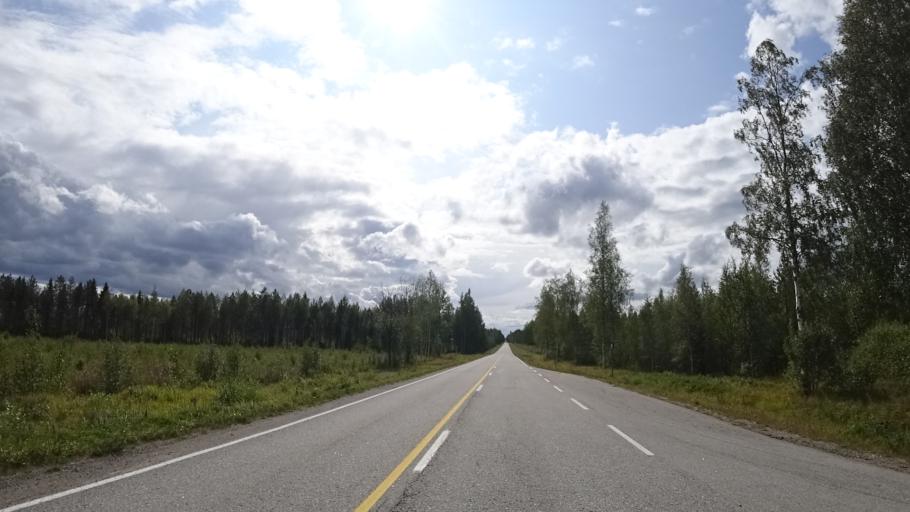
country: FI
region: North Karelia
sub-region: Joensuu
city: Ilomantsi
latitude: 62.7663
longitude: 31.0323
